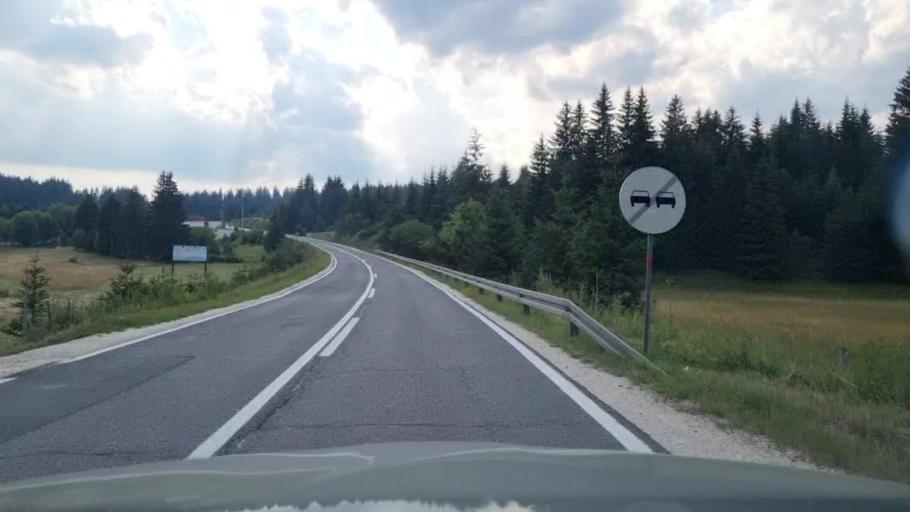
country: BA
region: Federation of Bosnia and Herzegovina
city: Olovo
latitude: 44.0793
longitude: 18.5150
